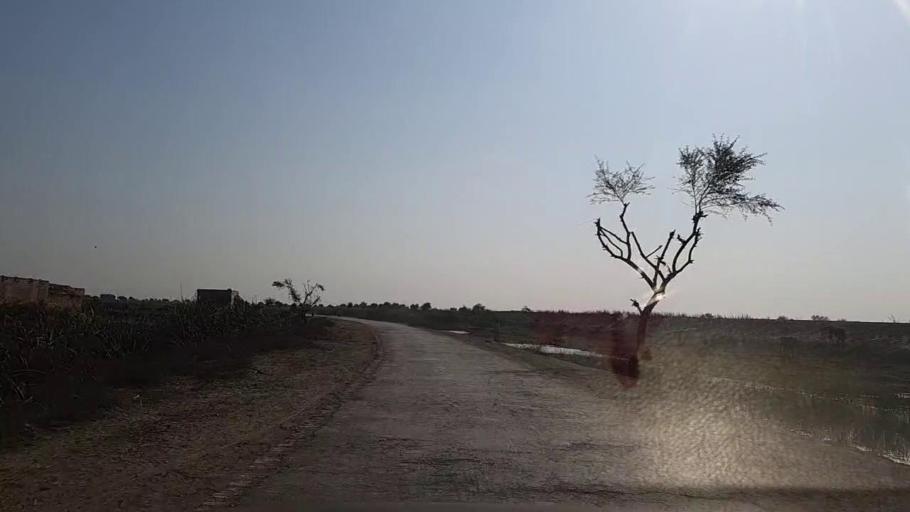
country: PK
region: Sindh
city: Sanghar
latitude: 25.9862
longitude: 69.0227
